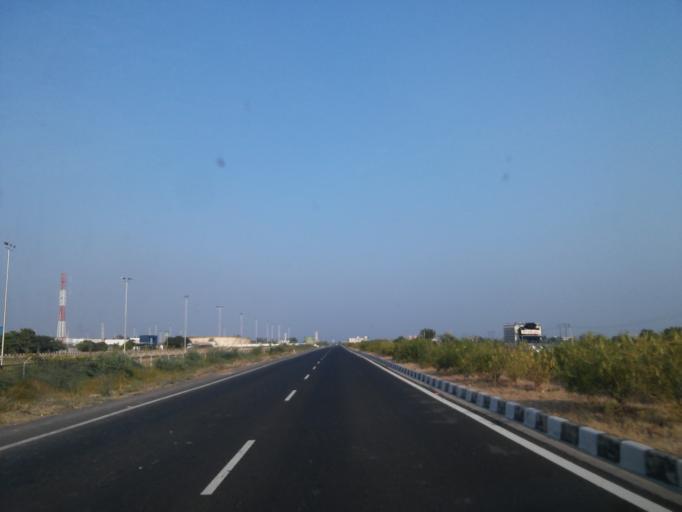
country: IN
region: Gujarat
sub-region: Ahmadabad
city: Mandal
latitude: 23.0957
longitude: 72.0456
